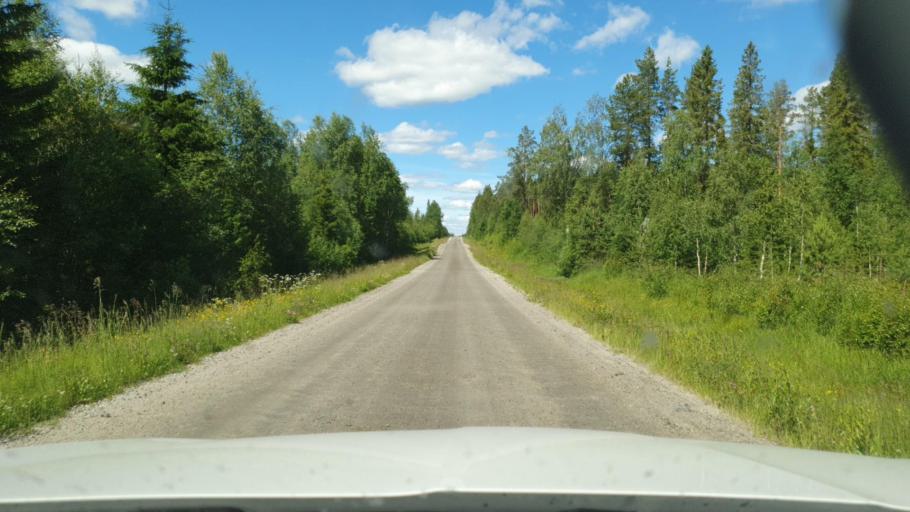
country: SE
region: Vaesterbotten
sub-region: Skelleftea Kommun
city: Byske
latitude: 65.1427
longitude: 21.1754
